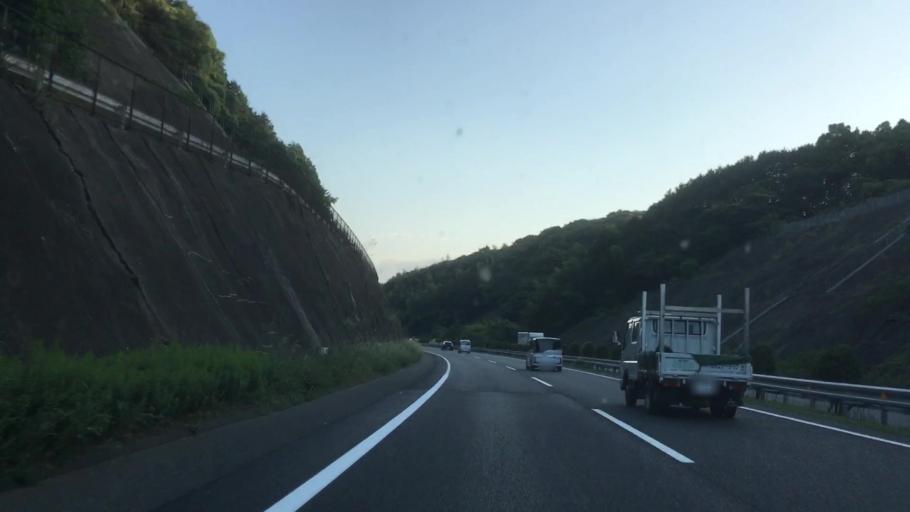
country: JP
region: Yamaguchi
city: Shimonoseki
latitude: 33.9037
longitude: 130.9715
